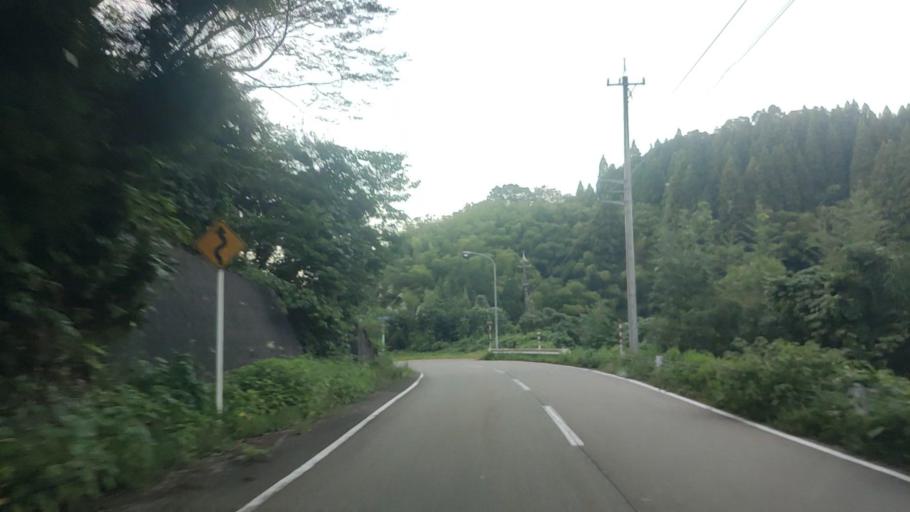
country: JP
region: Ishikawa
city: Tsubata
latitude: 36.6322
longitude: 136.7711
